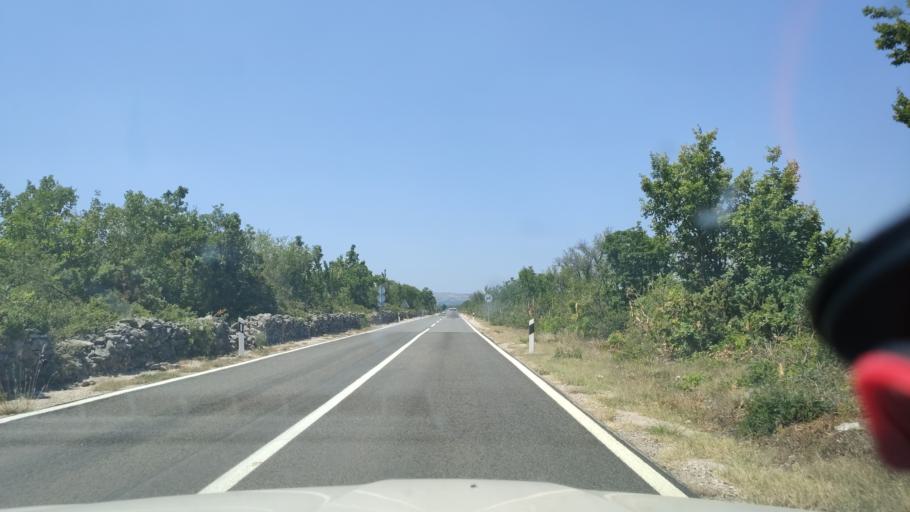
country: HR
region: Sibensko-Kniniska
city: Kistanje
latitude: 43.9726
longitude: 15.8966
